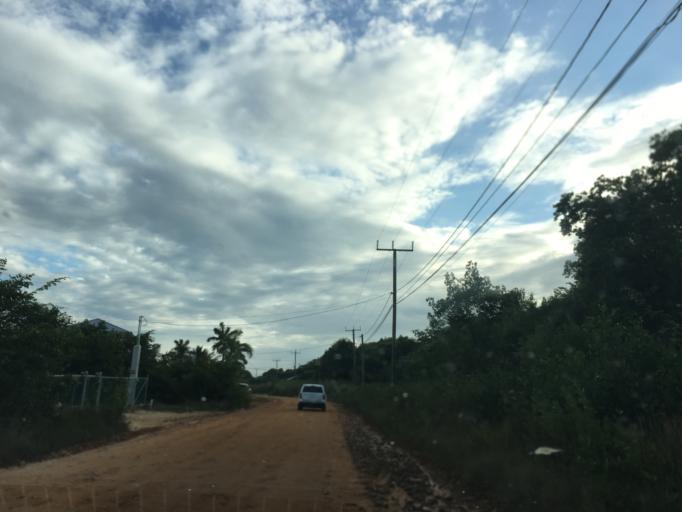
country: BZ
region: Stann Creek
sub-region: Dangriga
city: Dangriga
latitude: 16.8291
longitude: -88.2671
